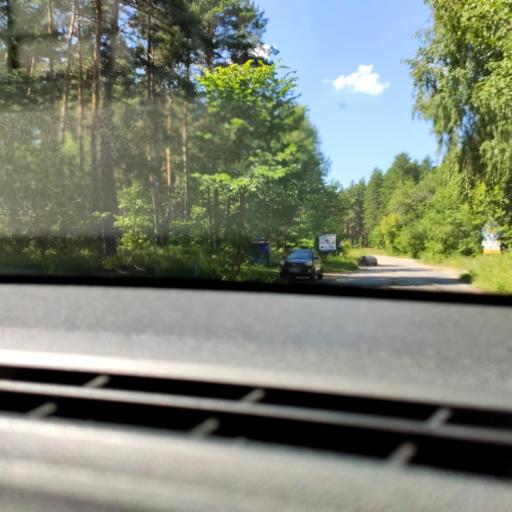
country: RU
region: Samara
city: Podstepki
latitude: 53.5711
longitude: 49.0299
